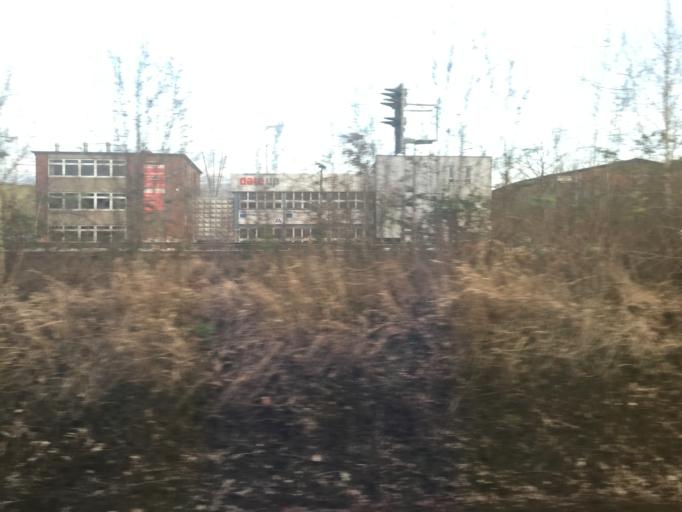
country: DE
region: Hamburg
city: Altona
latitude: 53.5701
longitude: 9.9337
